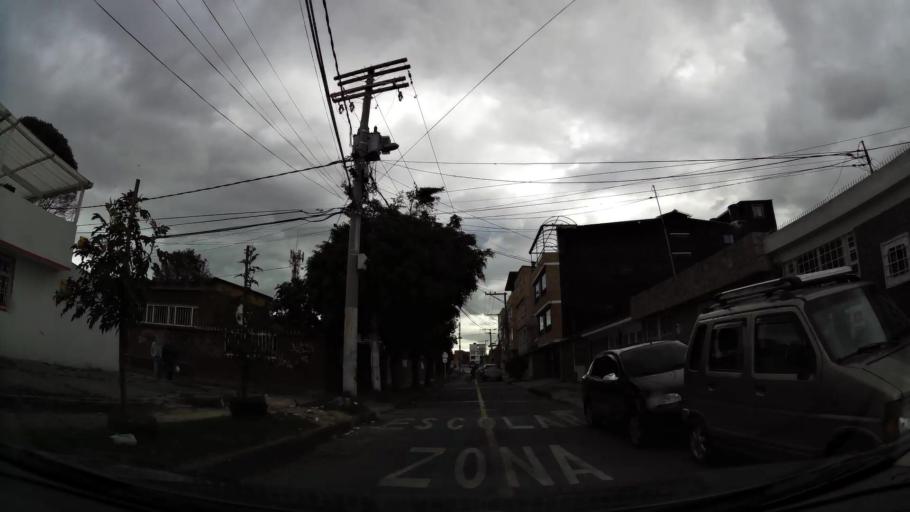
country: CO
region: Bogota D.C.
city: Barrio San Luis
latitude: 4.7060
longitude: -74.1099
